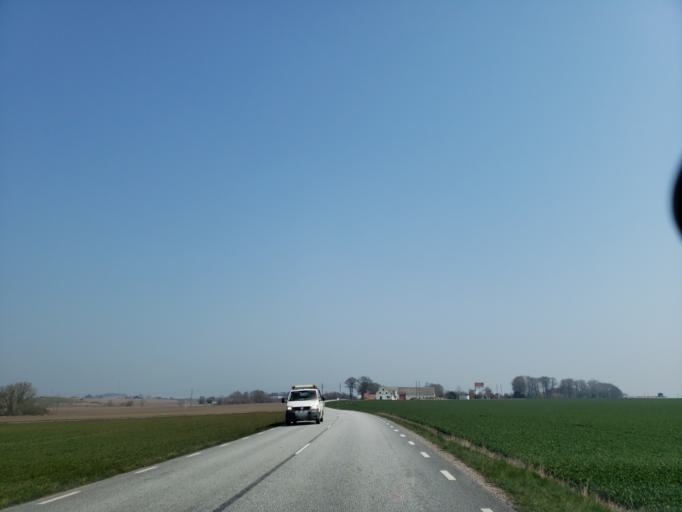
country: SE
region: Skane
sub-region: Simrishamns Kommun
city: Simrishamn
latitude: 55.4702
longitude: 14.2218
